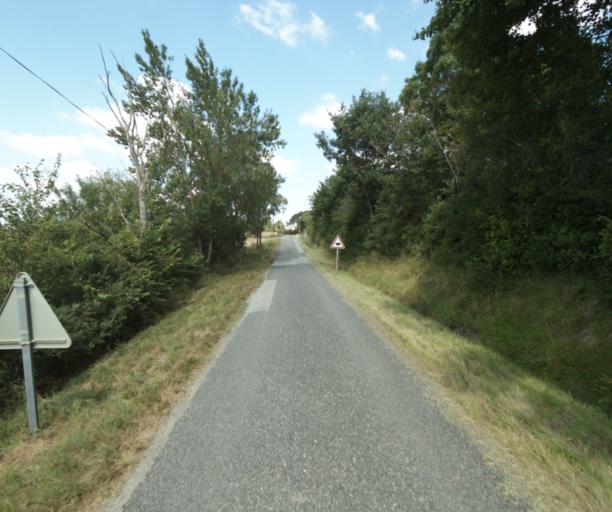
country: FR
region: Midi-Pyrenees
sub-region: Departement de la Haute-Garonne
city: Auriac-sur-Vendinelle
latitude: 43.4771
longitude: 1.8199
